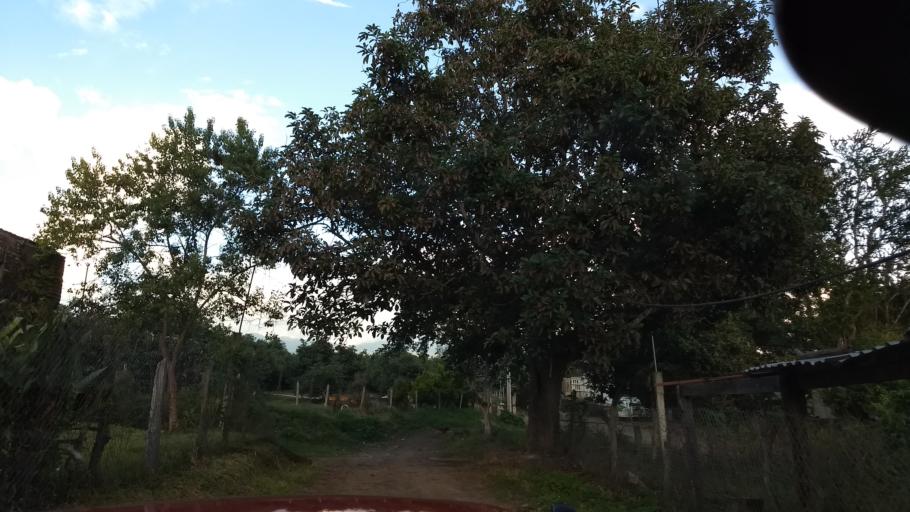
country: MX
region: Jalisco
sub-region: San Gabriel
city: Alista
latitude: 19.5108
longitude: -103.7520
